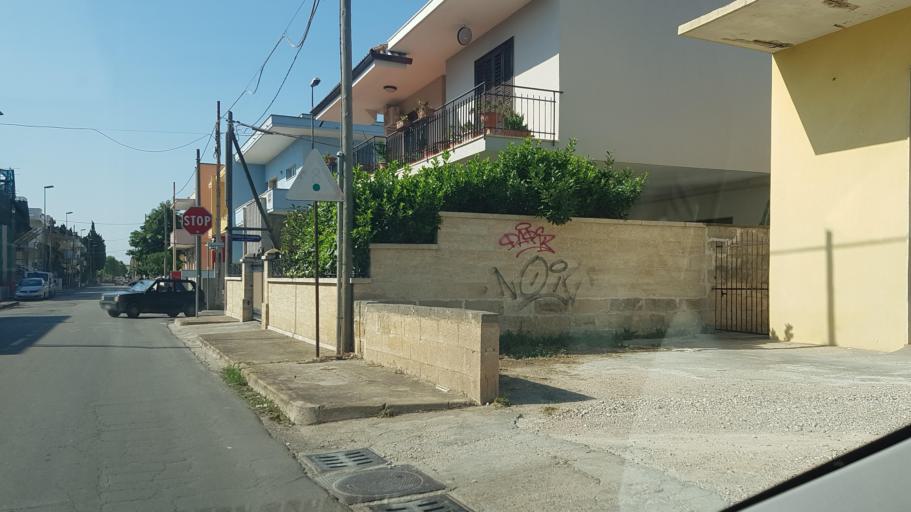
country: IT
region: Apulia
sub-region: Provincia di Lecce
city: Taurisano
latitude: 39.9497
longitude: 18.2184
